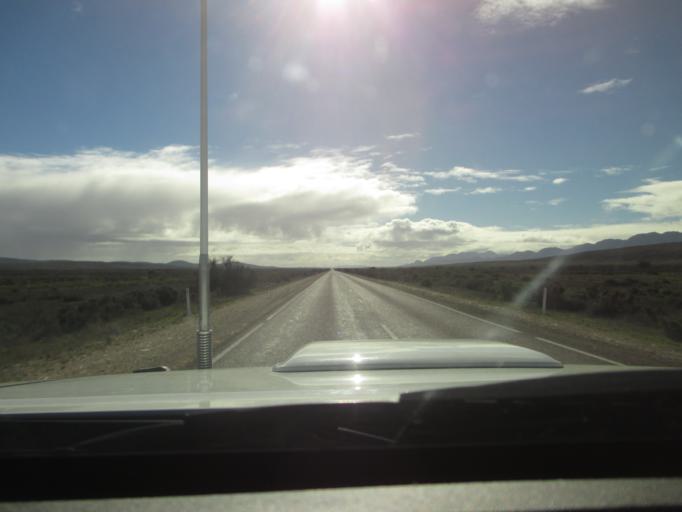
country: AU
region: South Australia
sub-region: Flinders Ranges
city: Quorn
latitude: -31.7291
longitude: 138.3438
